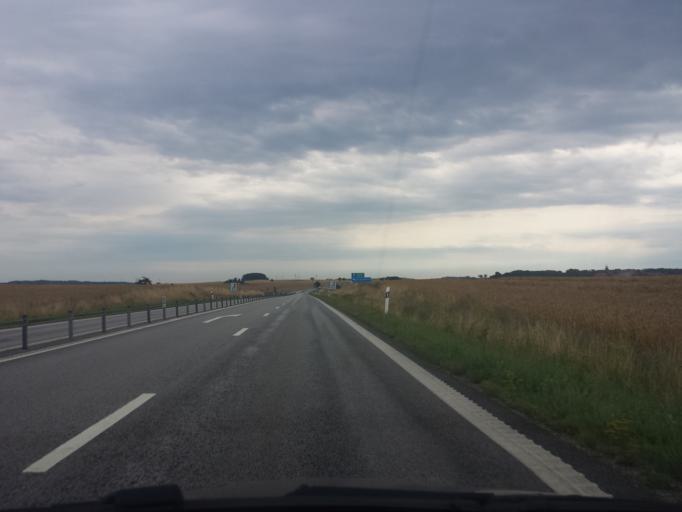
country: SE
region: Skane
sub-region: Skurups Kommun
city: Rydsgard
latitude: 55.4727
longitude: 13.6837
